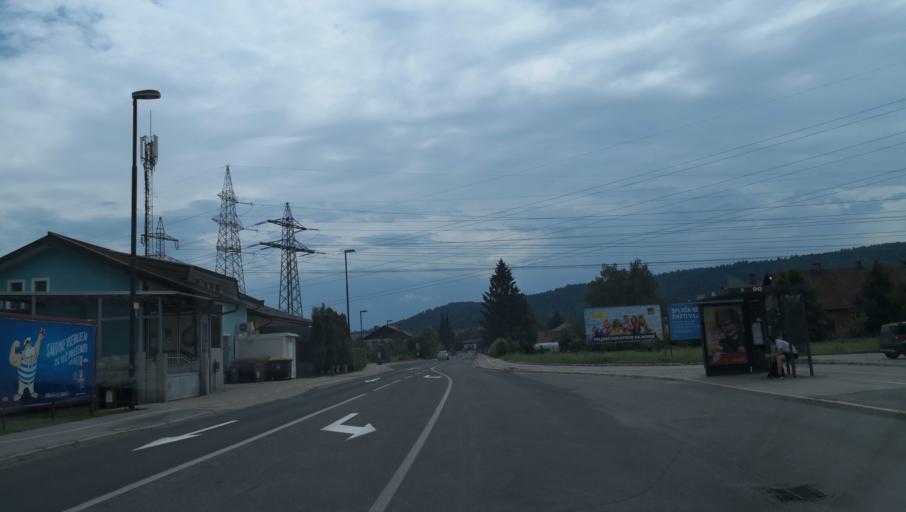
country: SI
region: Medvode
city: Zgornje Pirnice
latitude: 46.1133
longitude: 14.4617
